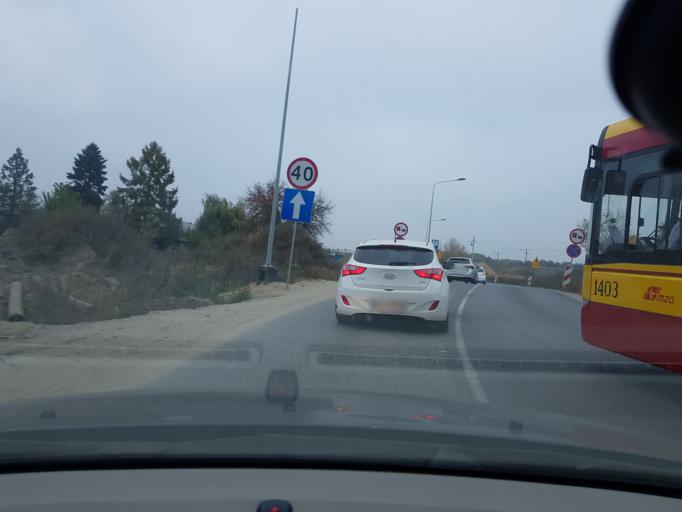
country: PL
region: Masovian Voivodeship
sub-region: Powiat pruszkowski
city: Nadarzyn
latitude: 52.0931
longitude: 20.8135
